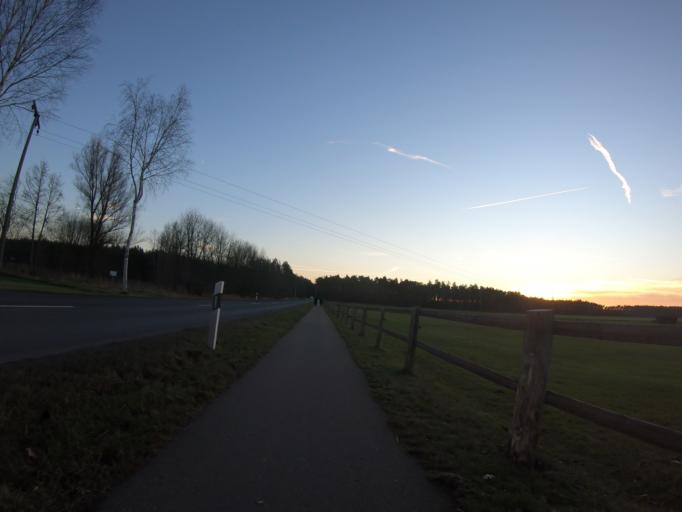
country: DE
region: Lower Saxony
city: Wagenhoff
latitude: 52.5058
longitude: 10.4817
